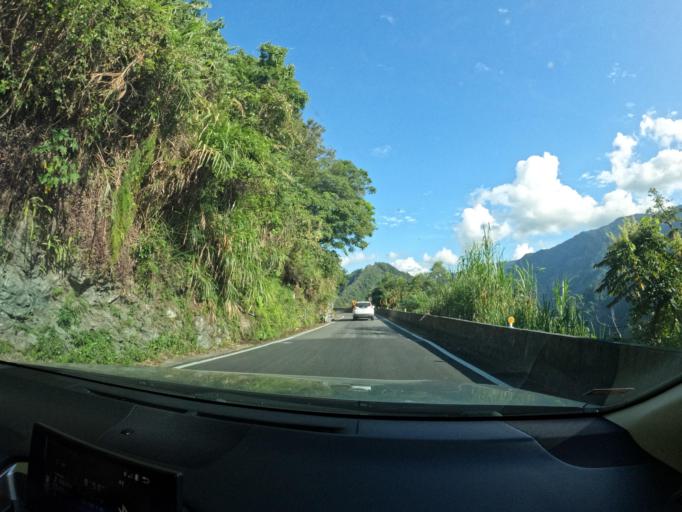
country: TW
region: Taiwan
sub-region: Taitung
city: Taitung
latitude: 23.1891
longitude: 121.0214
